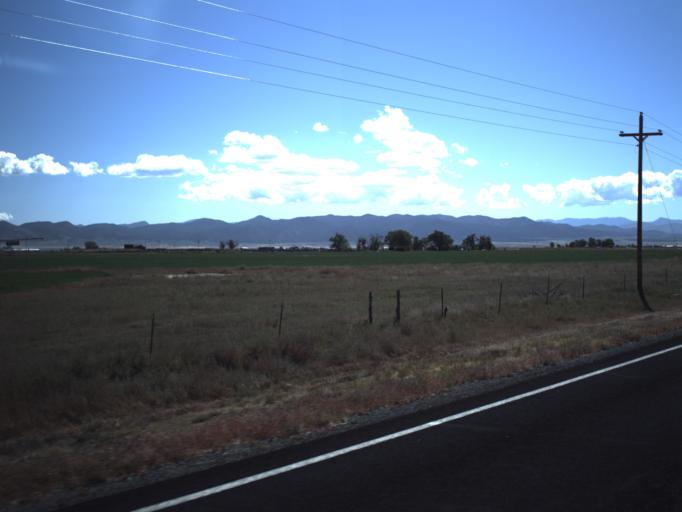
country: US
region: Utah
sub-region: Washington County
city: Enterprise
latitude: 37.7050
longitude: -113.6565
